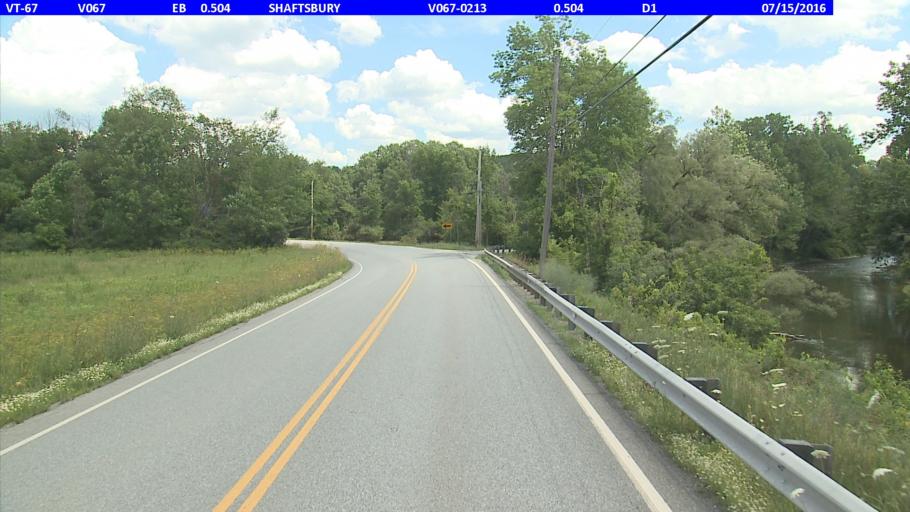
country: US
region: Vermont
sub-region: Bennington County
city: North Bennington
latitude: 42.9363
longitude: -73.2667
